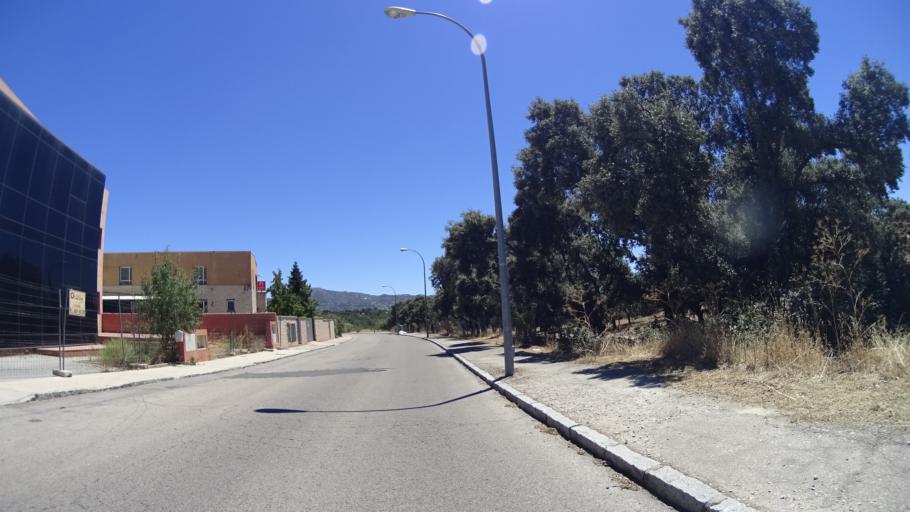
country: ES
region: Madrid
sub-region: Provincia de Madrid
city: Alpedrete
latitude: 40.6588
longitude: -4.0165
